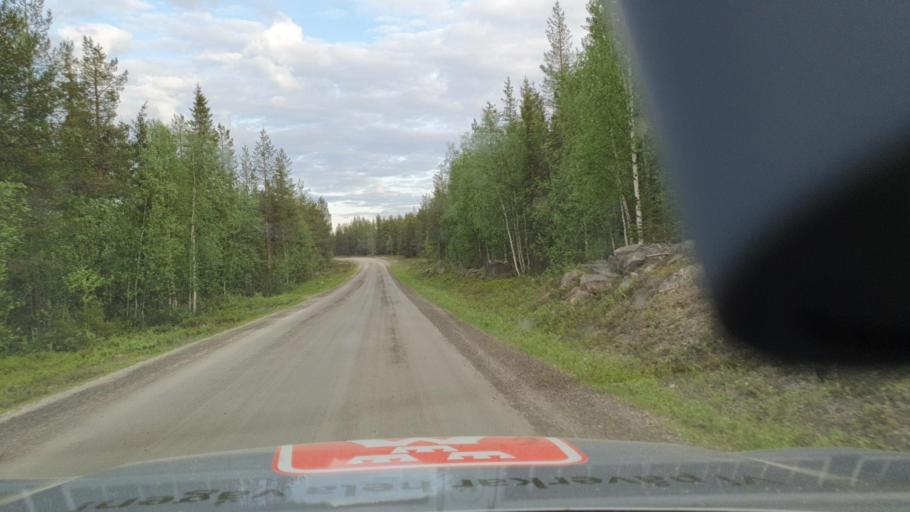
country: SE
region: Norrbotten
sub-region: Gallivare Kommun
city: Gaellivare
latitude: 66.7081
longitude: 21.1552
